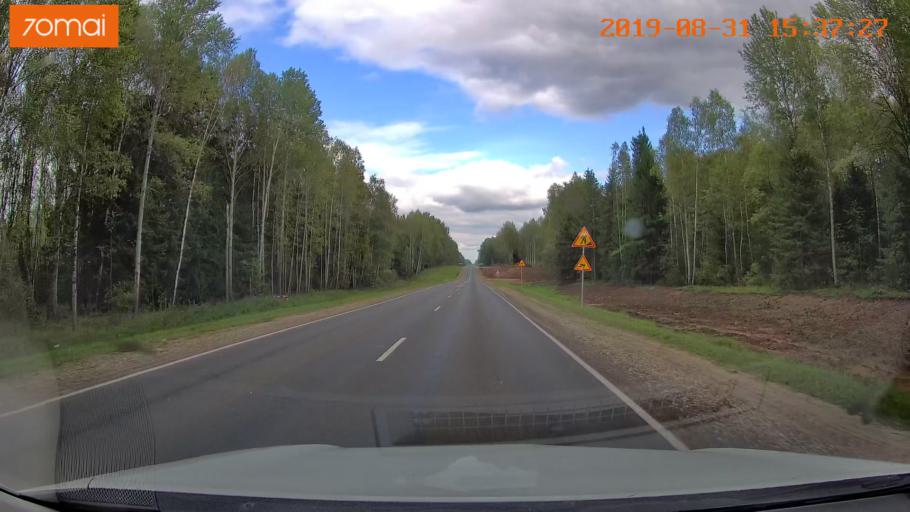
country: RU
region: Kaluga
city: Mosal'sk
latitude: 54.6183
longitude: 34.7846
